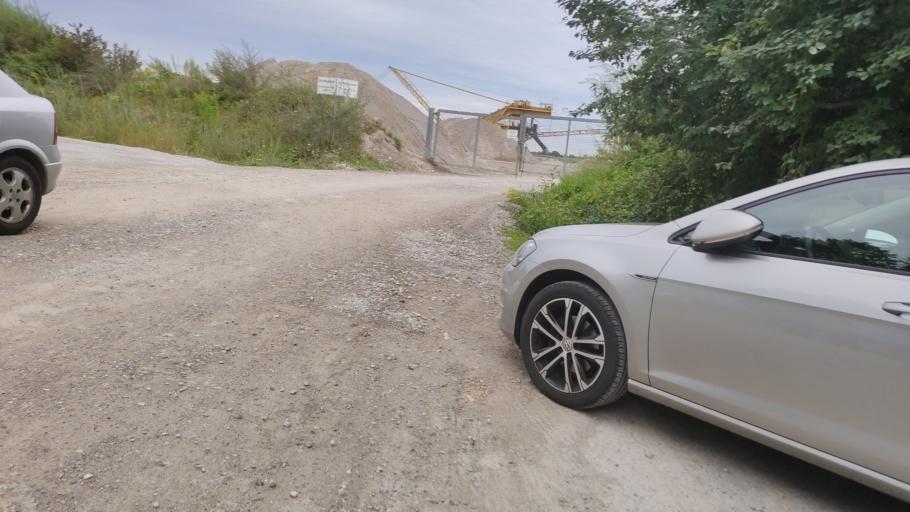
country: DE
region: Bavaria
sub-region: Swabia
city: Konigsbrunn
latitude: 48.2456
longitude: 10.8820
